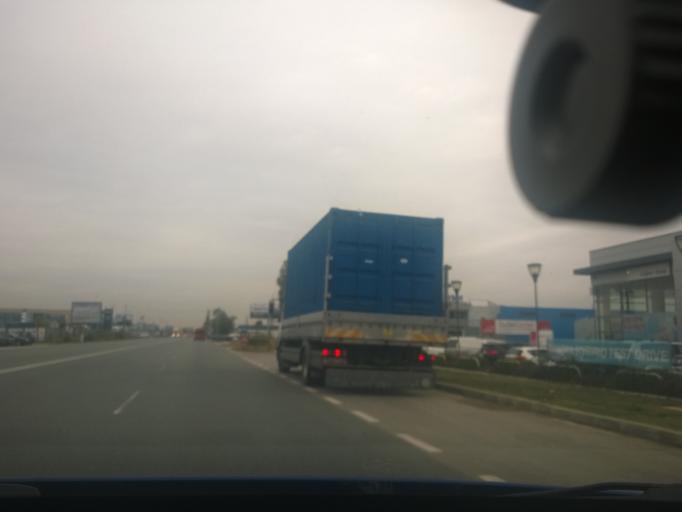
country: BG
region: Sofiya
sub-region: Obshtina Bozhurishte
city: Bozhurishte
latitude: 42.7404
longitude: 23.2378
